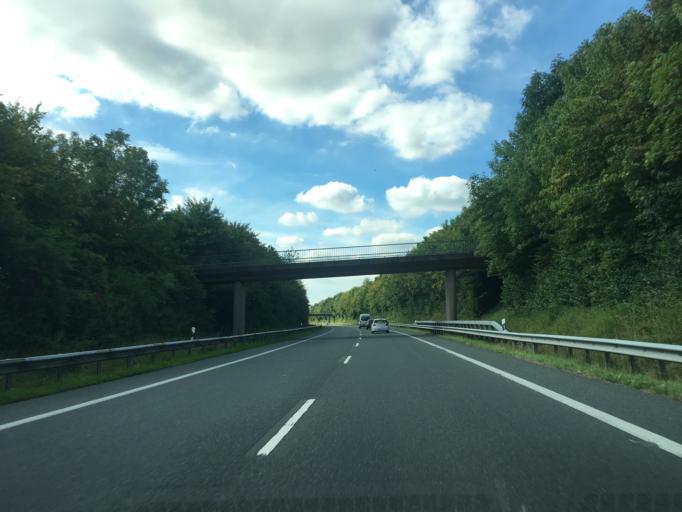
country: DE
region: North Rhine-Westphalia
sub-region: Regierungsbezirk Detmold
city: Dorentrup
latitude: 51.9775
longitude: 9.0188
